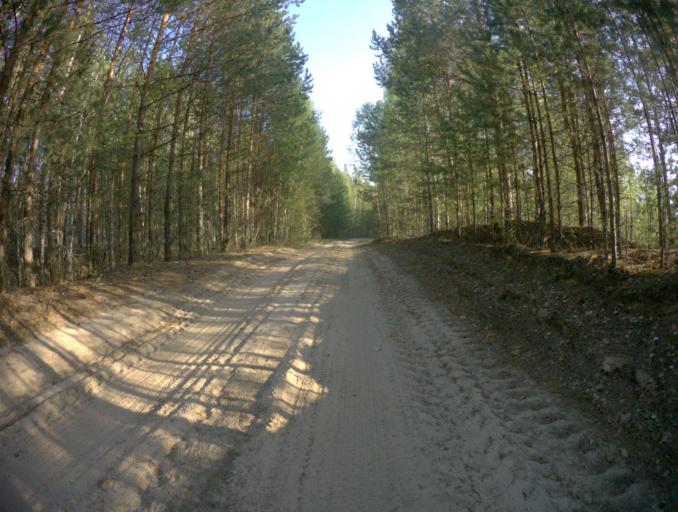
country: RU
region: Vladimir
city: Vyazniki
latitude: 56.3773
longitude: 42.1731
